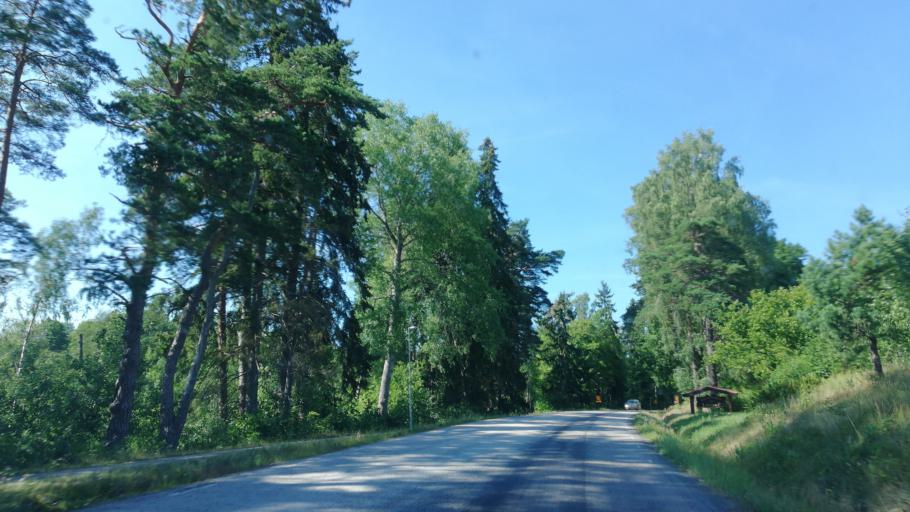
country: SE
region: OEstergoetland
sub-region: Finspangs Kommun
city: Finspang
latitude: 58.7305
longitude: 15.8280
